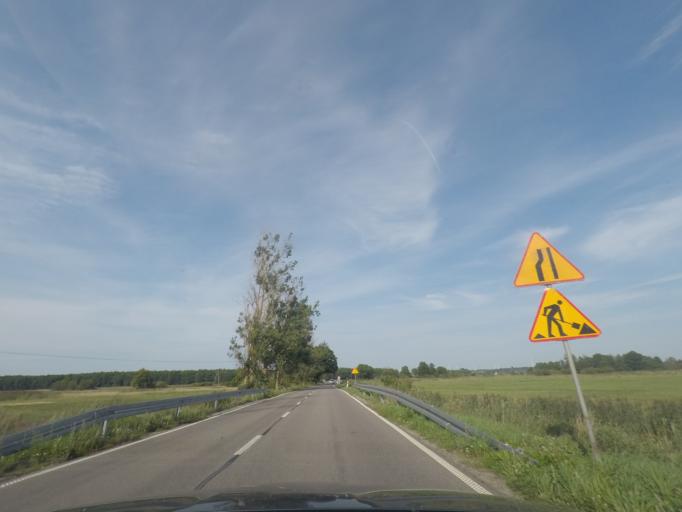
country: PL
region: Pomeranian Voivodeship
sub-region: Powiat leborski
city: Leba
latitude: 54.6531
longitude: 17.5616
